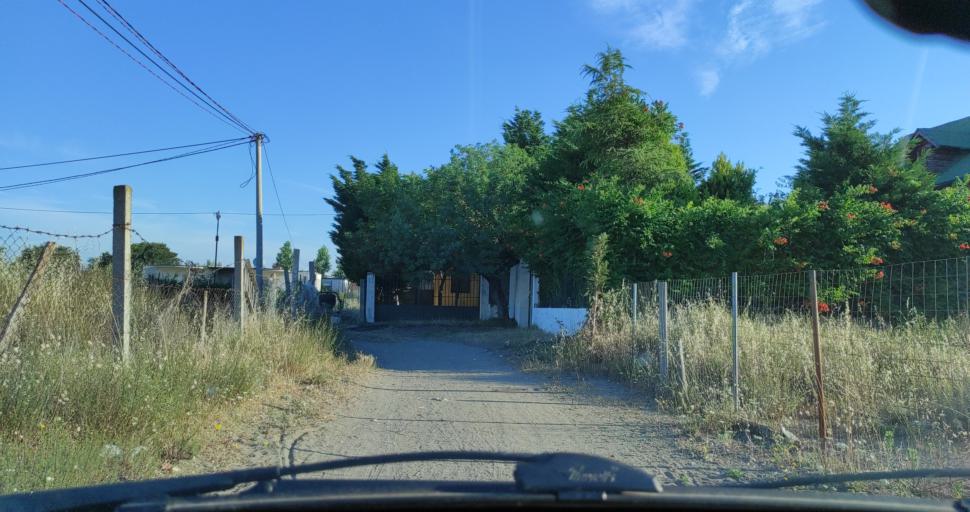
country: AL
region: Shkoder
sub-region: Rrethi i Shkodres
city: Velipoje
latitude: 41.8663
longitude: 19.4396
